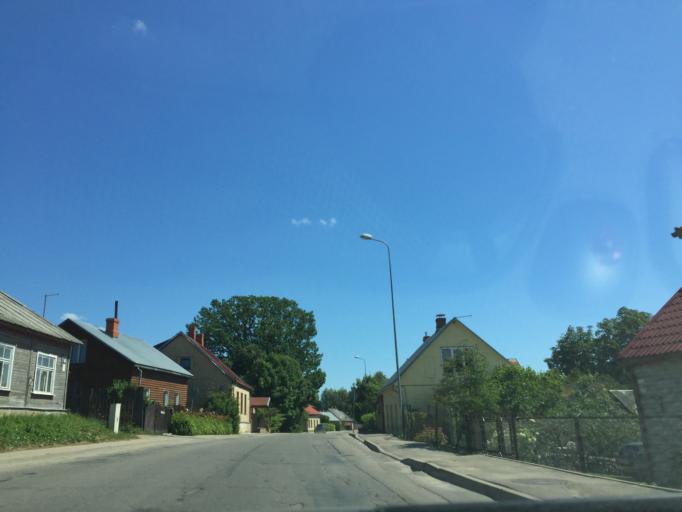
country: LV
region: Jekabpils Rajons
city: Jekabpils
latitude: 56.5038
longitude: 25.8838
